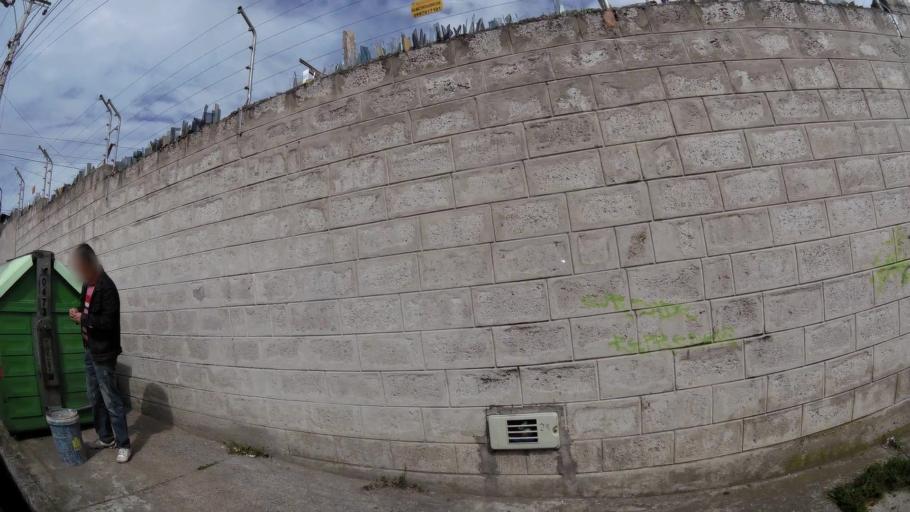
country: EC
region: Tungurahua
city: Ambato
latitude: -1.2457
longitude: -78.6201
